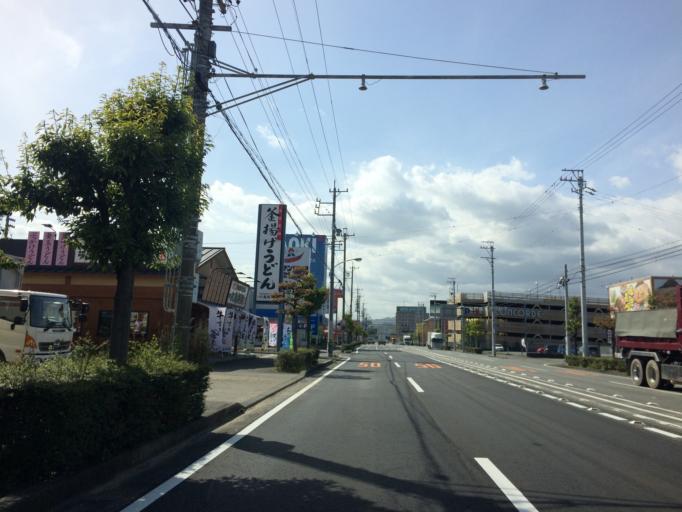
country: JP
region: Shizuoka
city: Yaizu
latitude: 34.8800
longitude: 138.3084
